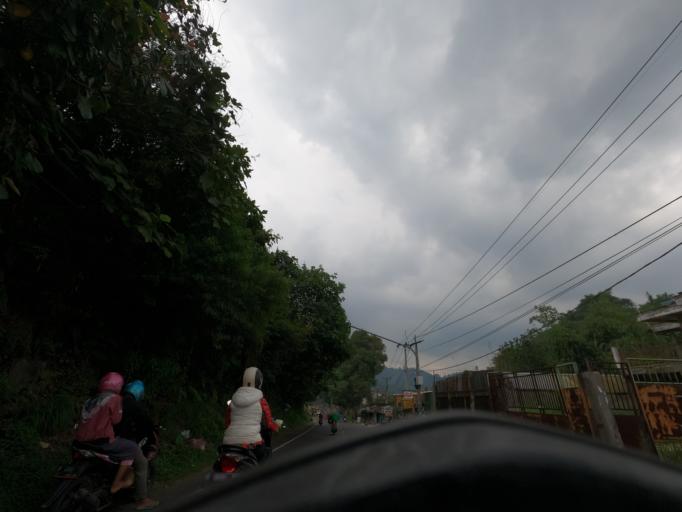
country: ID
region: West Java
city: Sukabumi
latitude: -6.7788
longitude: 107.0630
